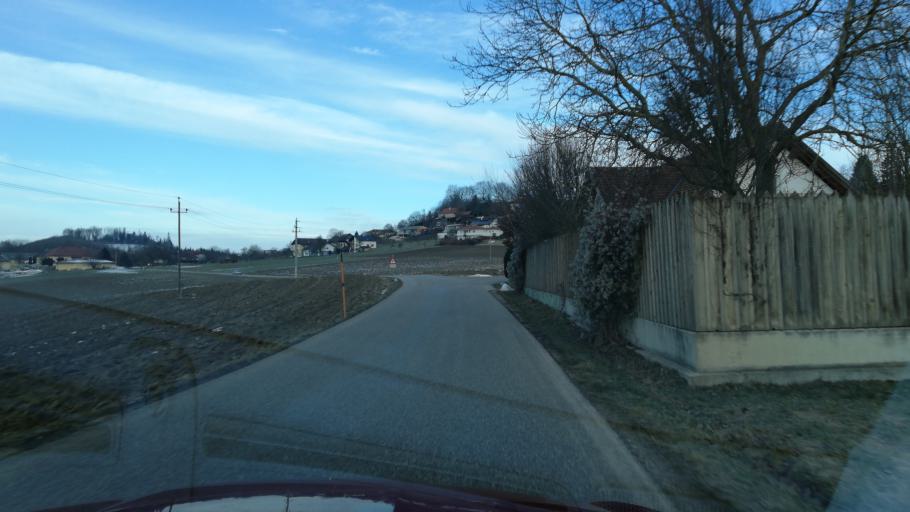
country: AT
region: Upper Austria
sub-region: Wels-Land
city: Buchkirchen
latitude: 48.2318
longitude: 14.0044
